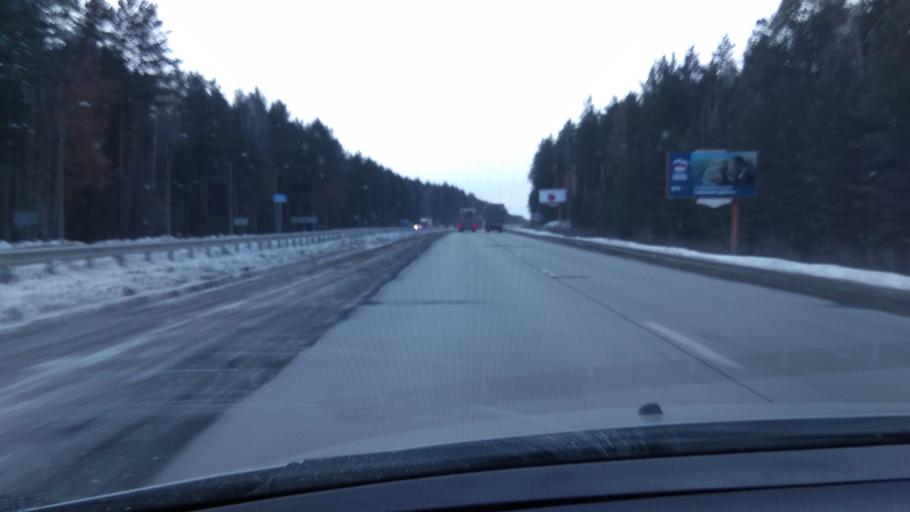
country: RU
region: Sverdlovsk
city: Sysert'
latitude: 56.5710
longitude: 60.8614
